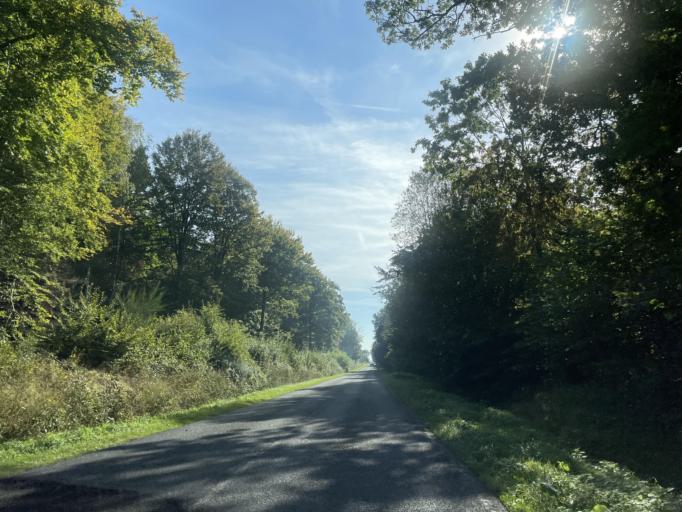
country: FR
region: Ile-de-France
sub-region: Departement de Seine-et-Marne
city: Saint-Jean-les-Deux-Jumeaux
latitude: 48.9143
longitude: 3.0147
